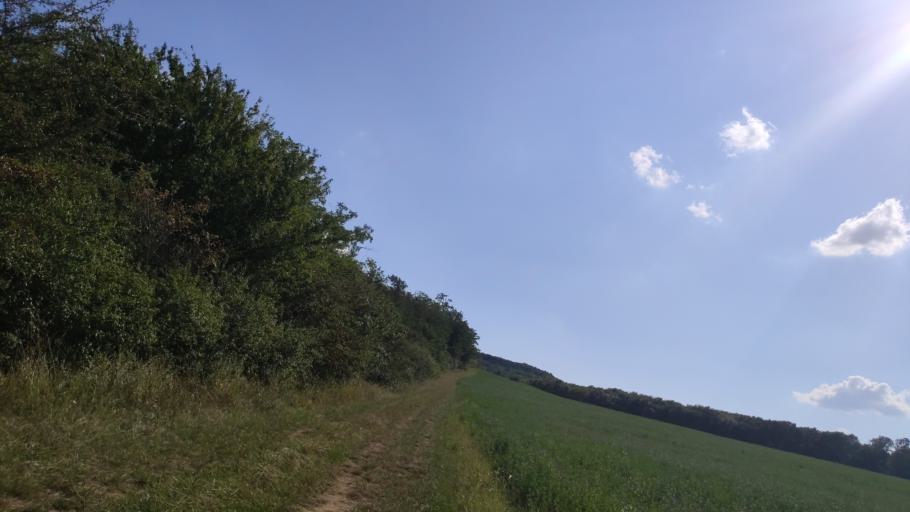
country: HU
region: Pest
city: Biatorbagy
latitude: 47.4684
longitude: 18.8581
